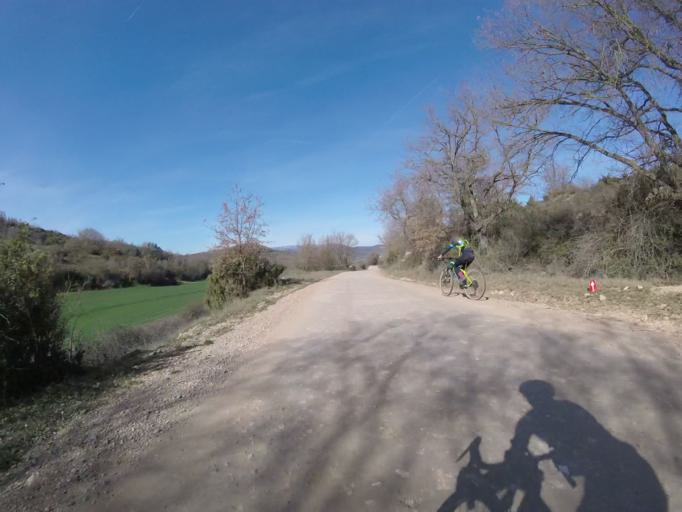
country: ES
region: Navarre
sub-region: Provincia de Navarra
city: Oteiza
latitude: 42.6465
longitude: -1.9658
